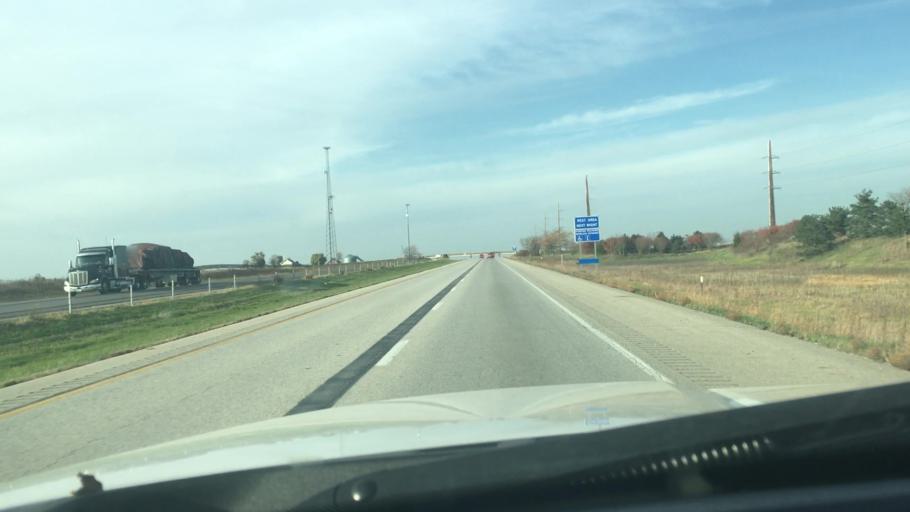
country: US
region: Iowa
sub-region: Story County
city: Huxley
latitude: 41.8149
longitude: -93.5706
